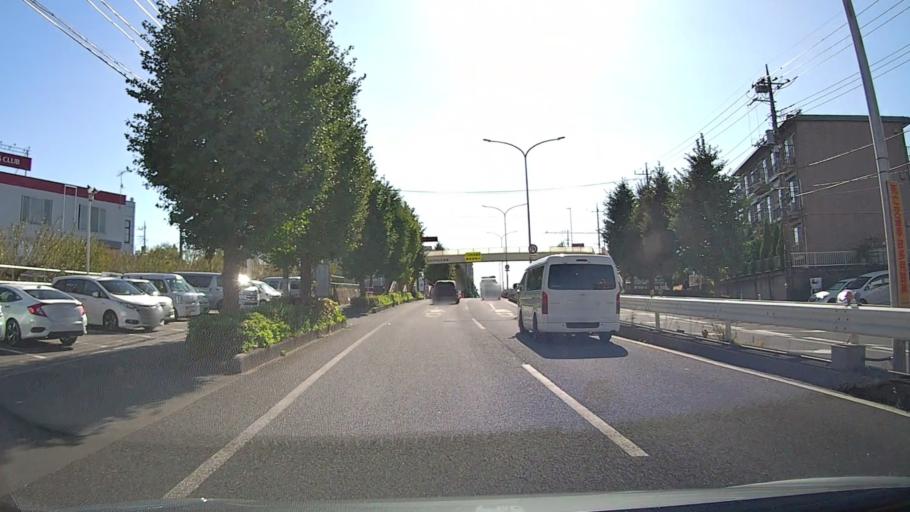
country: JP
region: Saitama
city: Wako
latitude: 35.7698
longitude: 139.6202
